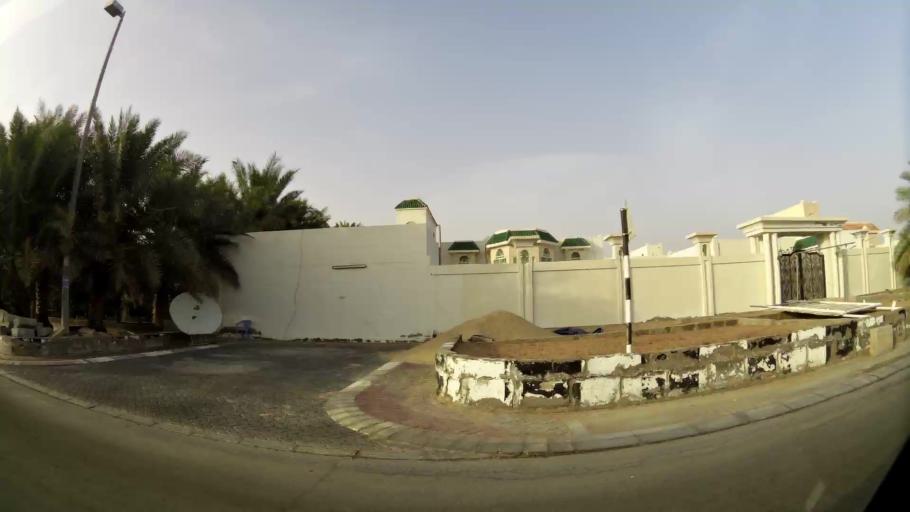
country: AE
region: Abu Dhabi
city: Al Ain
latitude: 24.1076
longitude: 55.7081
